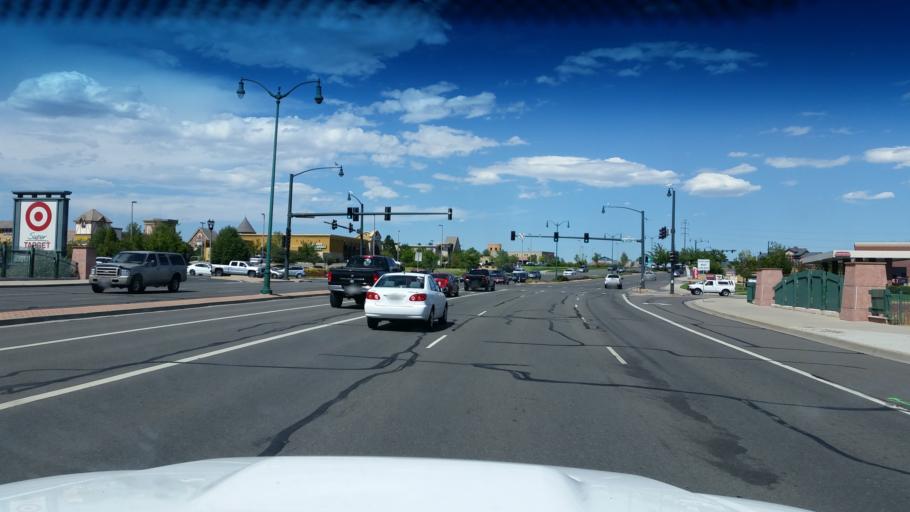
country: US
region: Colorado
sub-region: Broomfield County
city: Broomfield
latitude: 39.8847
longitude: -105.0753
